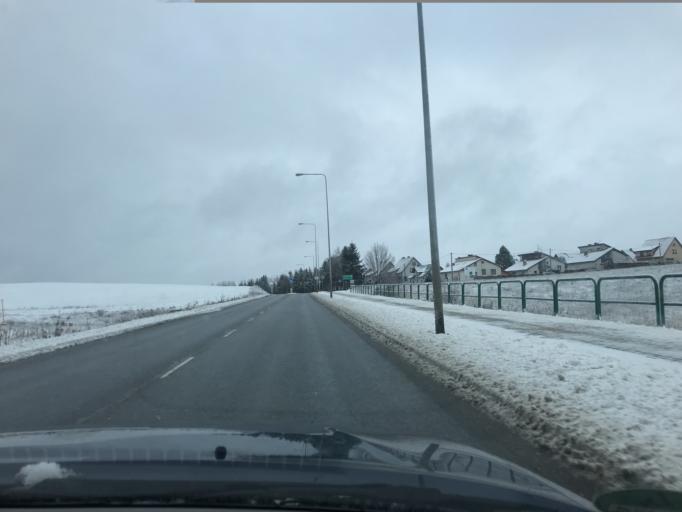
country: PL
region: Pomeranian Voivodeship
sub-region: Powiat bytowski
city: Bytow
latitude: 54.1870
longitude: 17.5089
